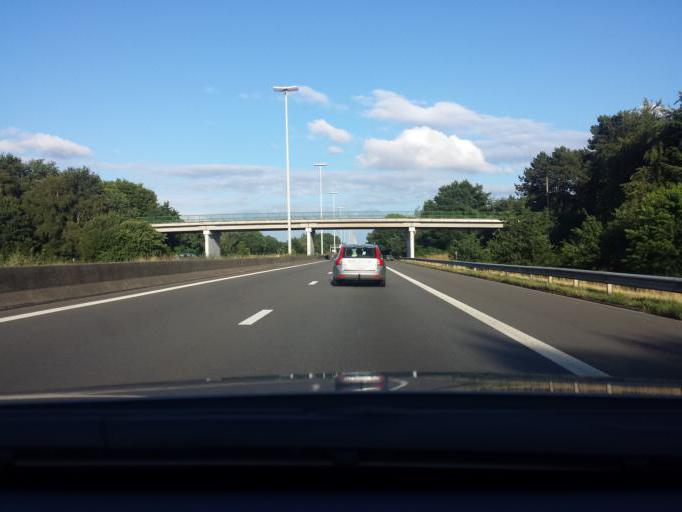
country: BE
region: Flanders
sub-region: Provincie Antwerpen
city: Herentals
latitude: 51.1542
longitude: 4.8355
